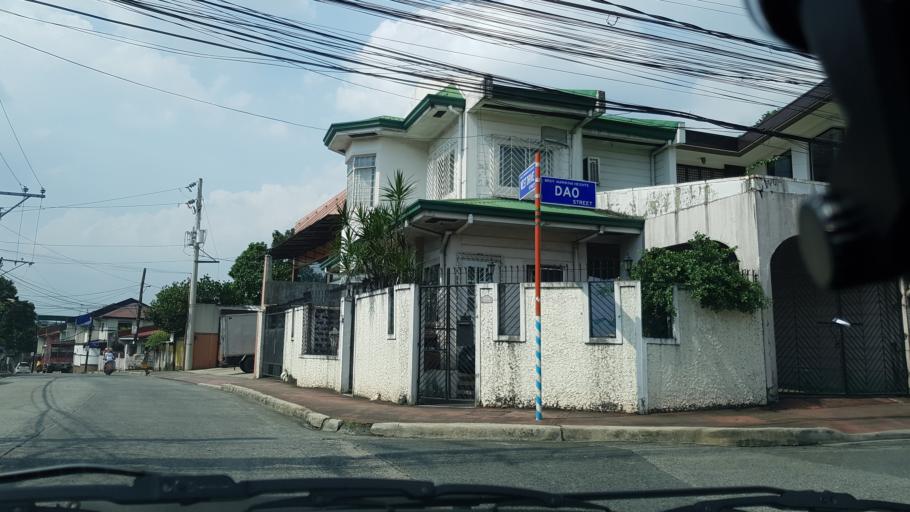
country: PH
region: Calabarzon
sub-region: Province of Rizal
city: Antipolo
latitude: 14.6548
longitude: 121.1161
